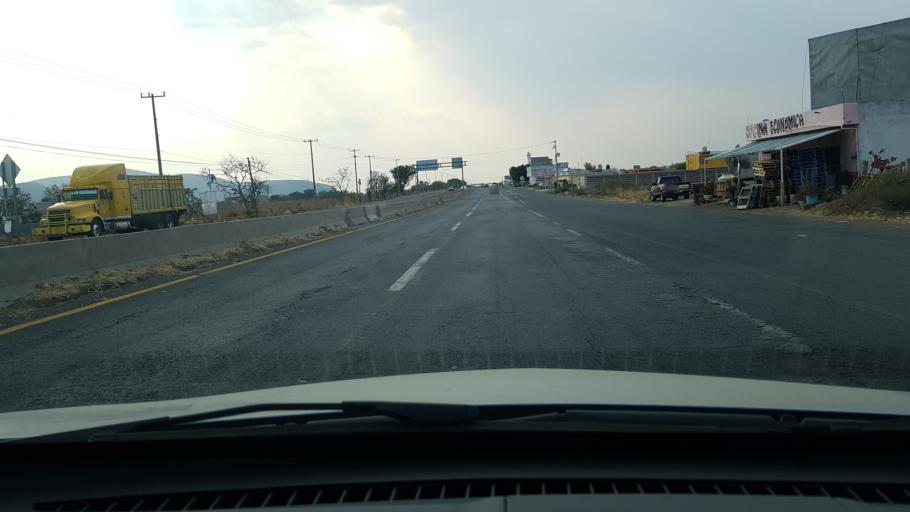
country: MX
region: Morelos
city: Amayuca
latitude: 18.7343
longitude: -98.8183
